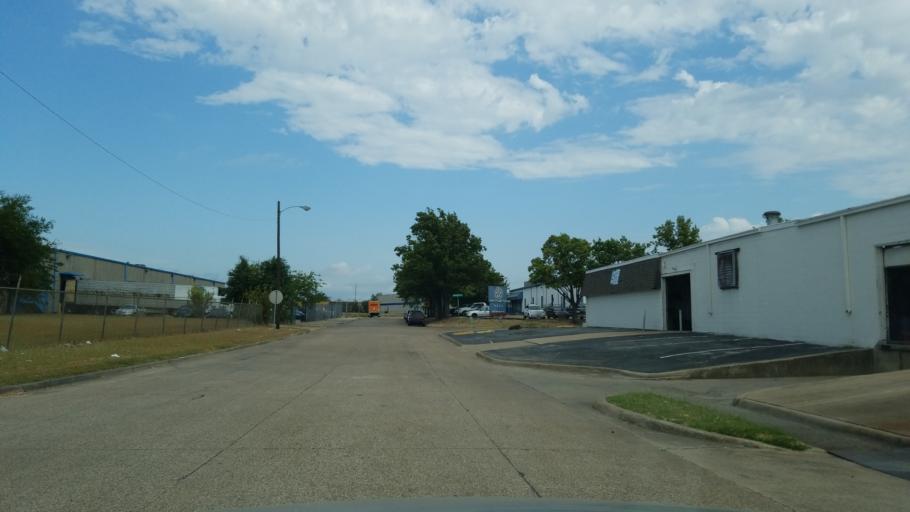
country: US
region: Texas
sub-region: Dallas County
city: Garland
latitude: 32.9011
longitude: -96.6907
